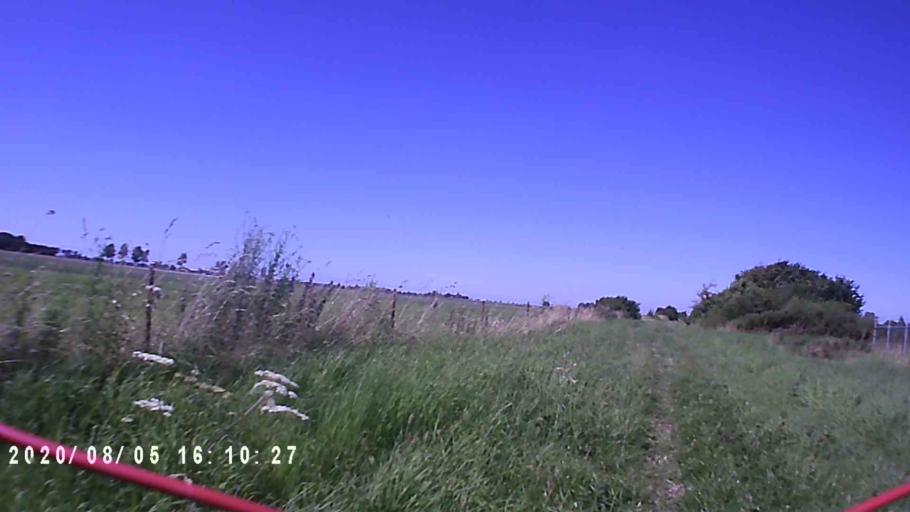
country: NL
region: Groningen
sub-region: Gemeente Winsum
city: Winsum
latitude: 53.3960
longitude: 6.5204
